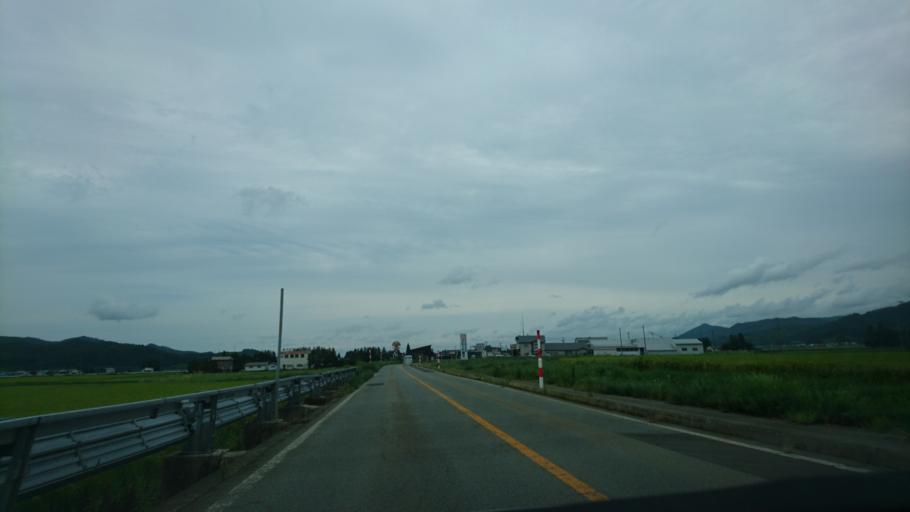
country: JP
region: Akita
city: Yuzawa
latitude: 39.1577
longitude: 140.5644
